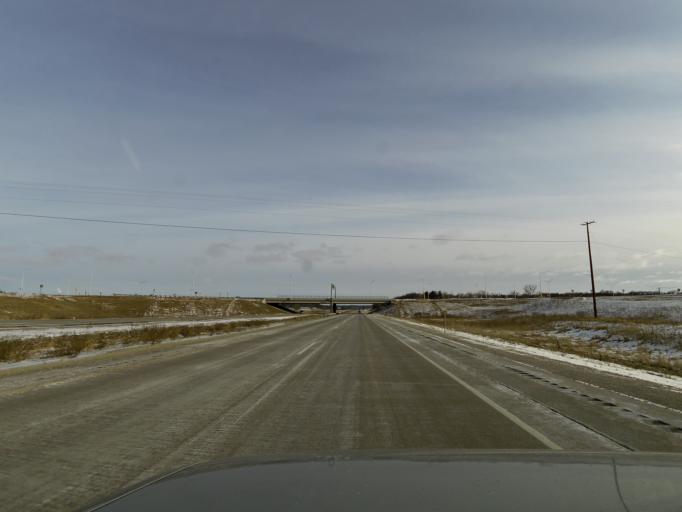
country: US
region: Wisconsin
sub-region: Pierce County
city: River Falls
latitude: 44.8994
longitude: -92.6506
